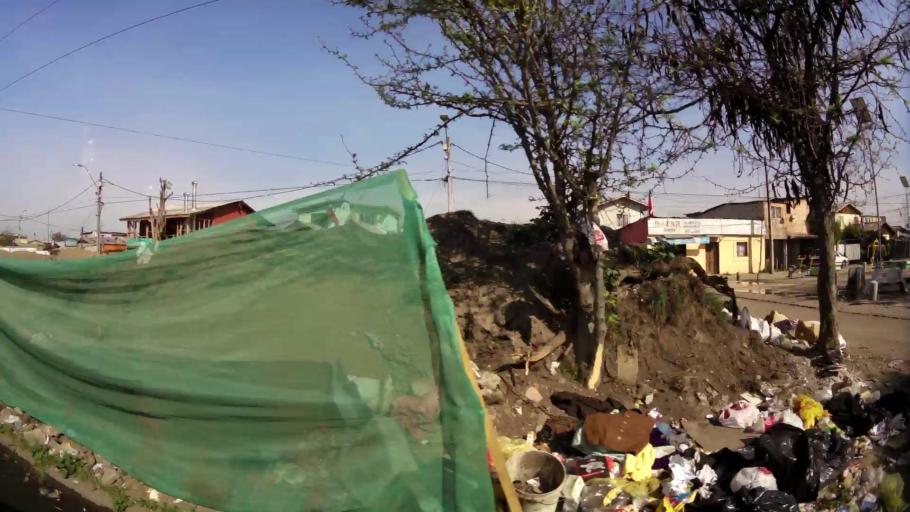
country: CL
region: Santiago Metropolitan
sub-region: Provincia de Santiago
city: Lo Prado
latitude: -33.4198
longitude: -70.7330
